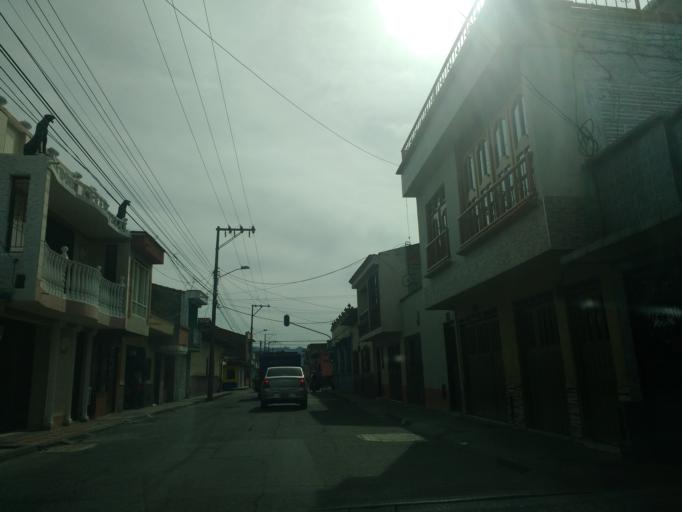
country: CO
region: Valle del Cauca
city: Cartago
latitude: 4.7487
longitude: -75.9049
